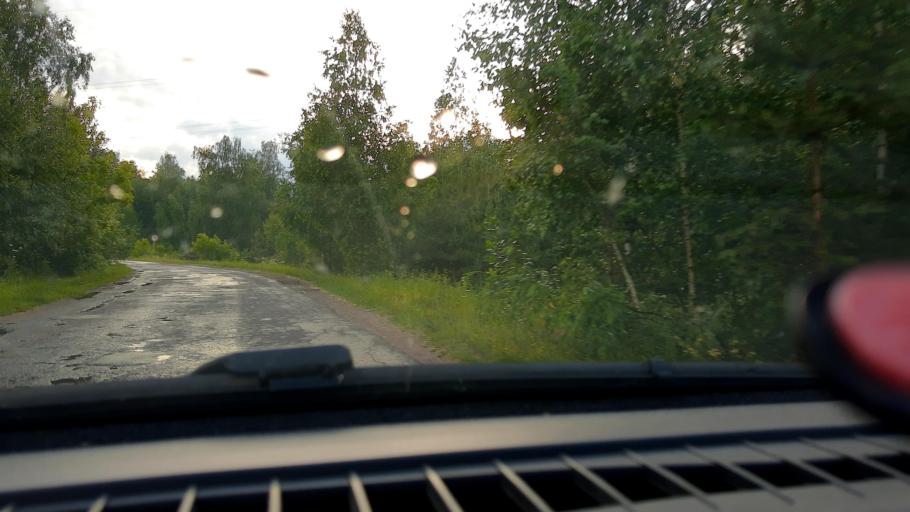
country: RU
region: Nizjnij Novgorod
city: Zavolzh'ye
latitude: 56.6757
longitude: 43.4160
